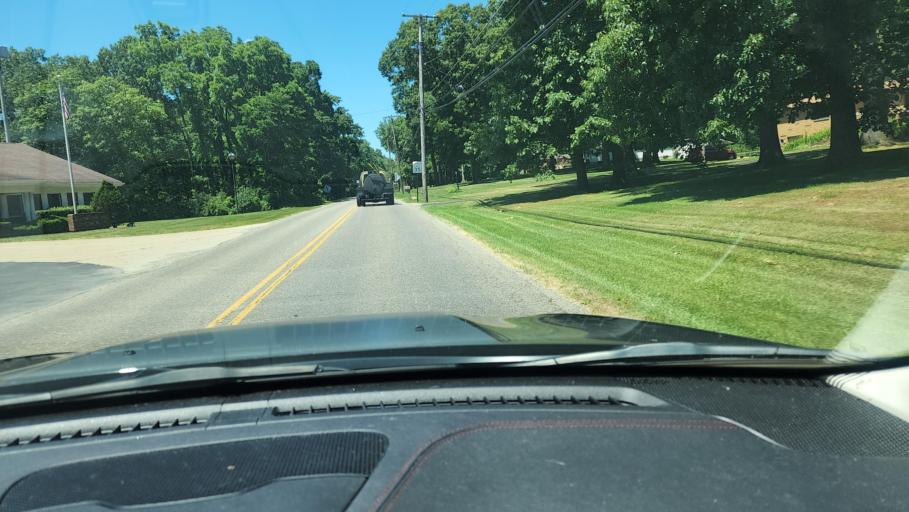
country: US
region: Ohio
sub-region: Mahoning County
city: Austintown
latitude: 41.0842
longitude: -80.7900
